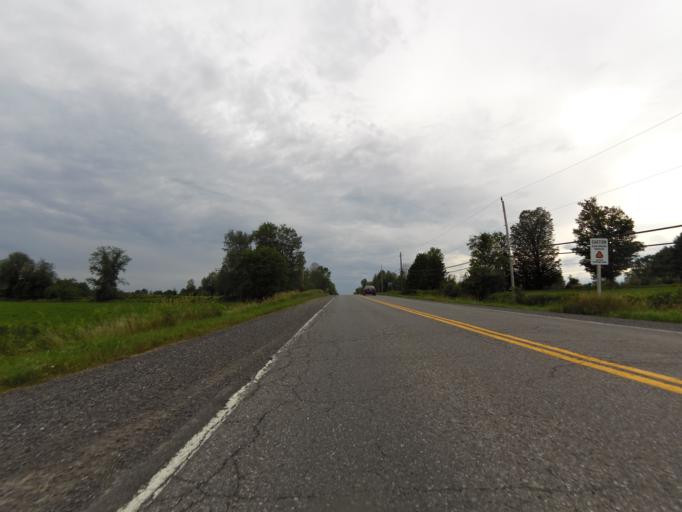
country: CA
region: Ontario
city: Carleton Place
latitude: 45.1562
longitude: -76.3012
